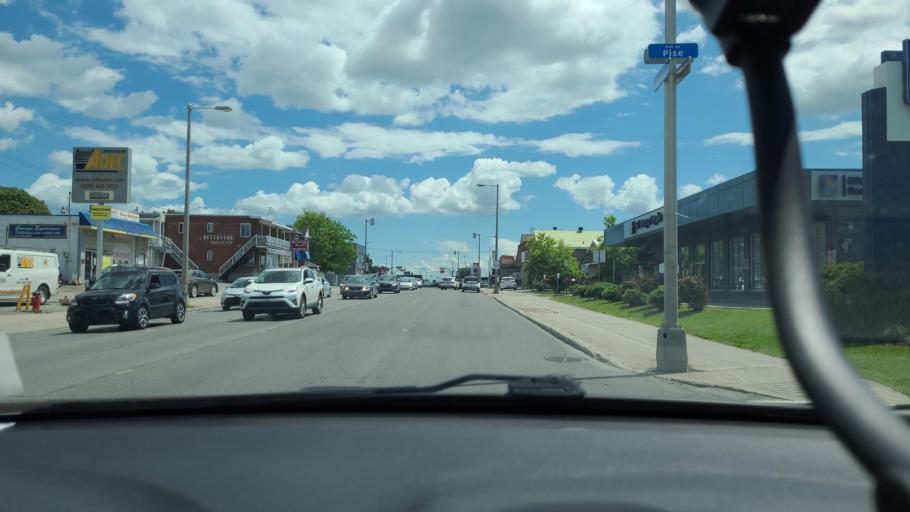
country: CA
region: Quebec
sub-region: Laval
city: Laval
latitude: 45.6046
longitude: -73.7303
